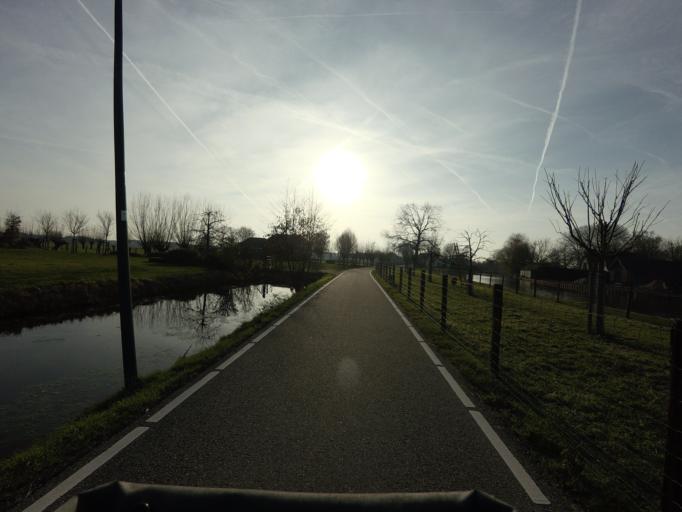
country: NL
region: Utrecht
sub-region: Gemeente Woerden
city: Woerden
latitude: 52.0974
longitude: 4.9149
